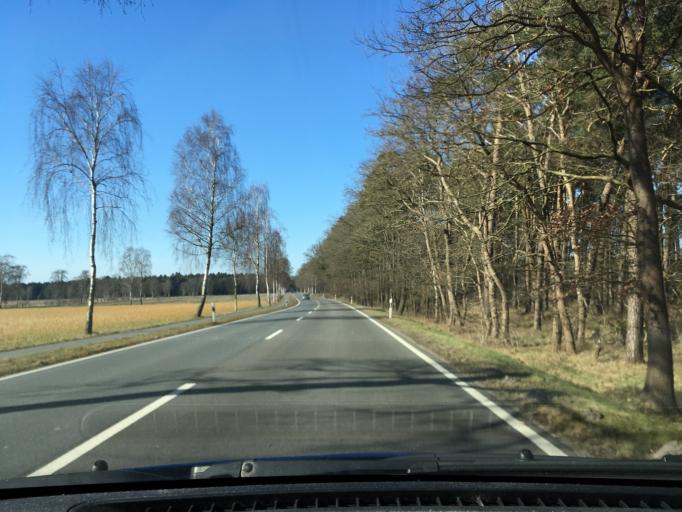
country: DE
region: Lower Saxony
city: Hemslingen
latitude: 53.0890
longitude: 9.5801
